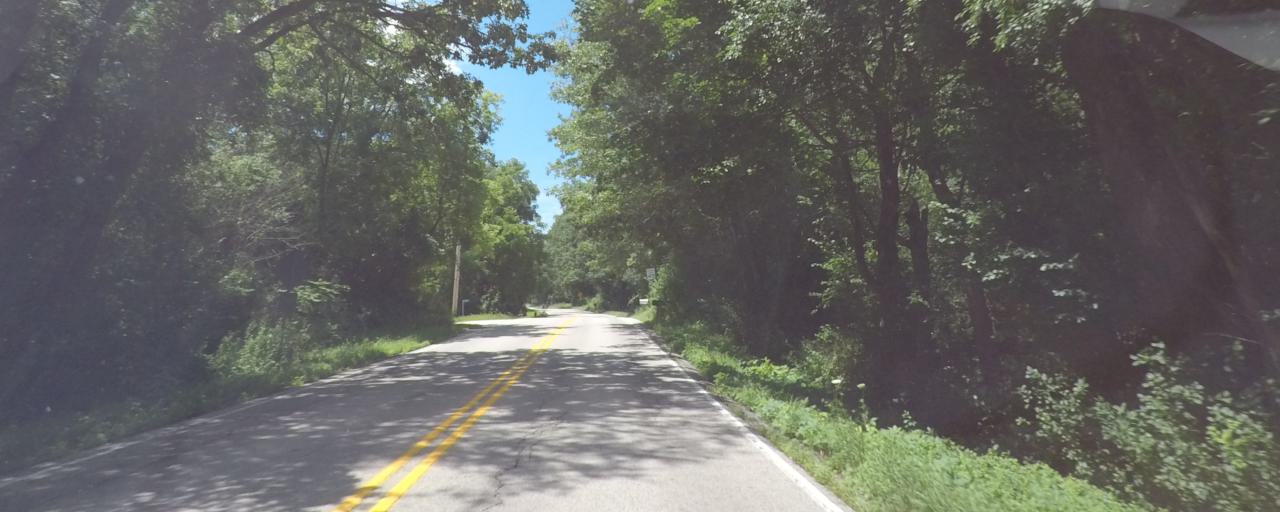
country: US
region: Wisconsin
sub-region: Waukesha County
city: Wales
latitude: 42.9874
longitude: -88.4128
